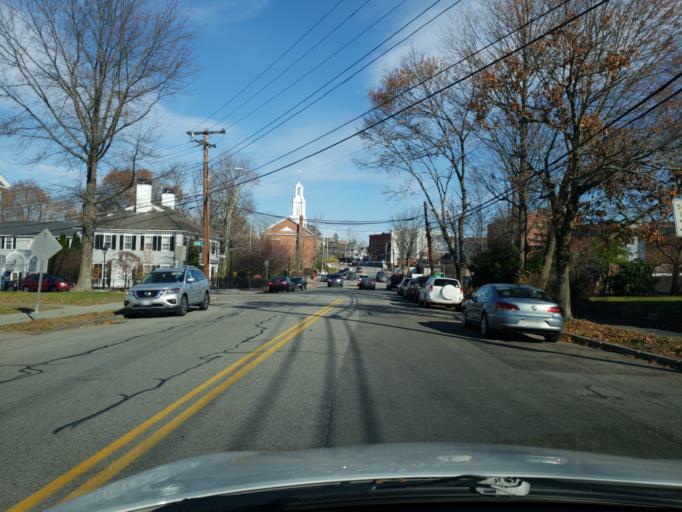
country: US
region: Massachusetts
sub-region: Essex County
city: Andover
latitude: 42.6548
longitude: -71.1420
